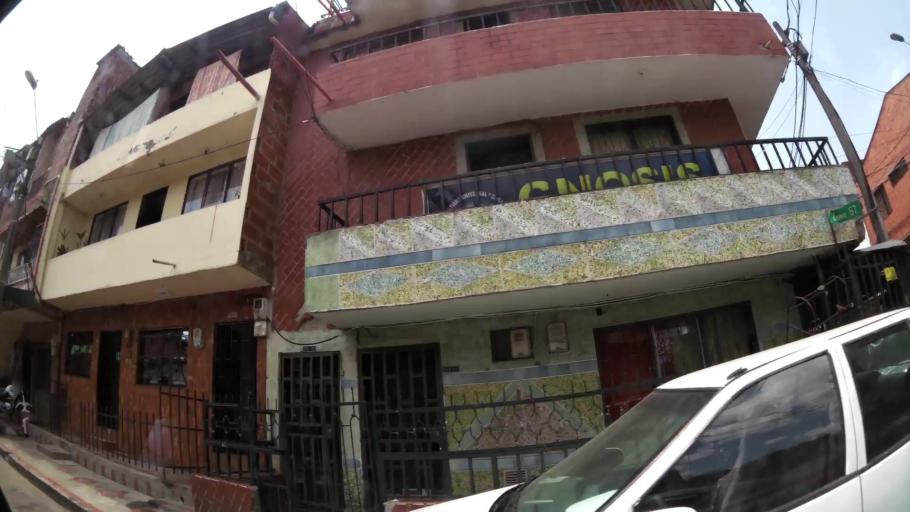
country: CO
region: Antioquia
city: Bello
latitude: 6.2970
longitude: -75.5691
